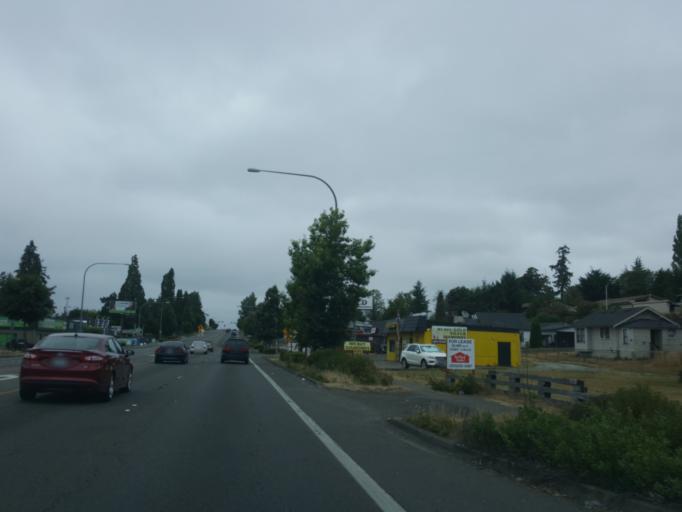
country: US
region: Washington
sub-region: Pierce County
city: Parkland
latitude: 47.1480
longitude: -122.4343
